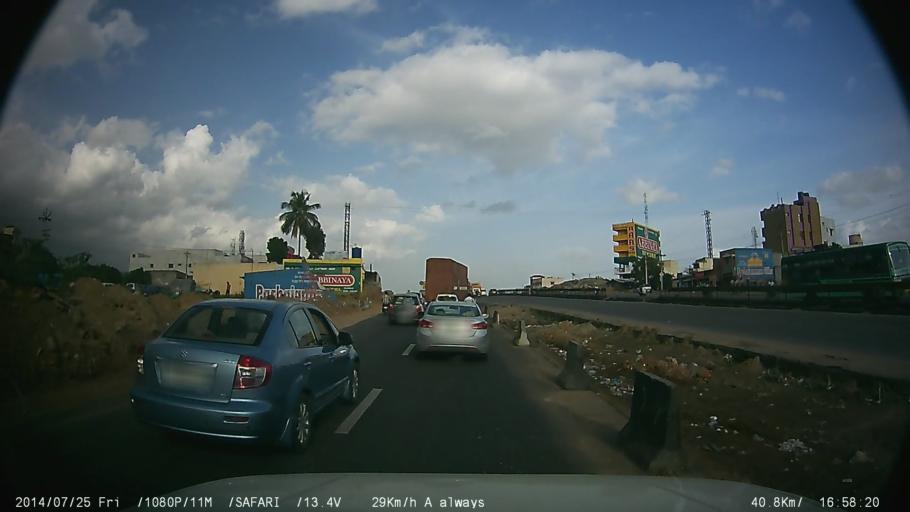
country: IN
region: Tamil Nadu
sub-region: Krishnagiri
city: Hosur
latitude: 12.7292
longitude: 77.8414
